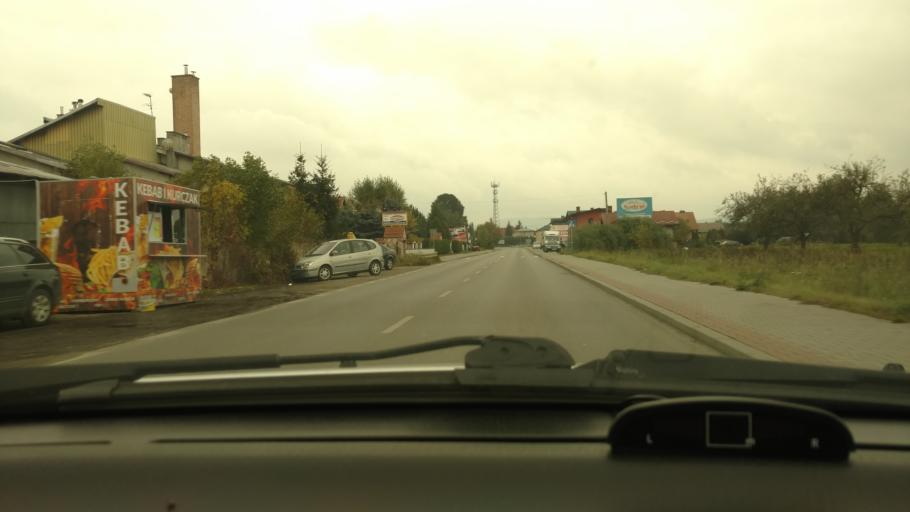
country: PL
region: Lesser Poland Voivodeship
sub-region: Powiat nowosadecki
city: Chelmiec
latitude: 49.6228
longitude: 20.6675
